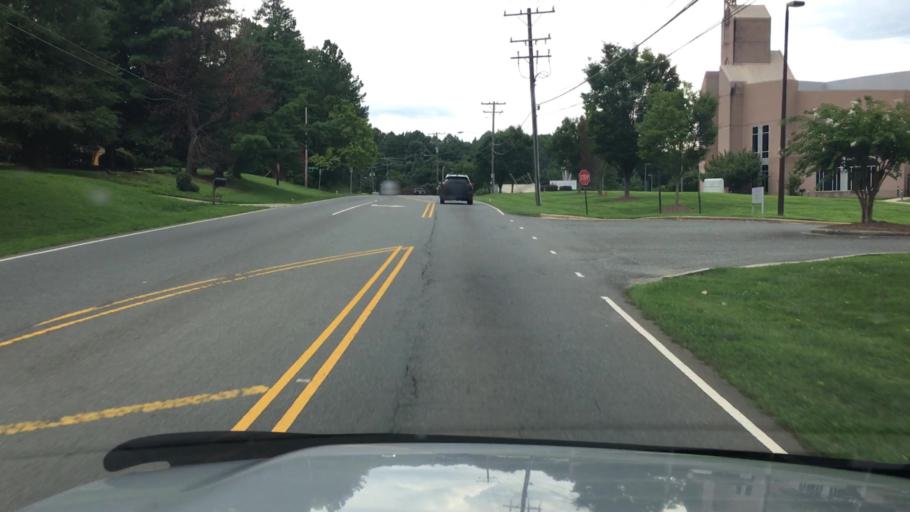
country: US
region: North Carolina
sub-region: Mecklenburg County
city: Charlotte
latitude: 35.3182
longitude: -80.8648
